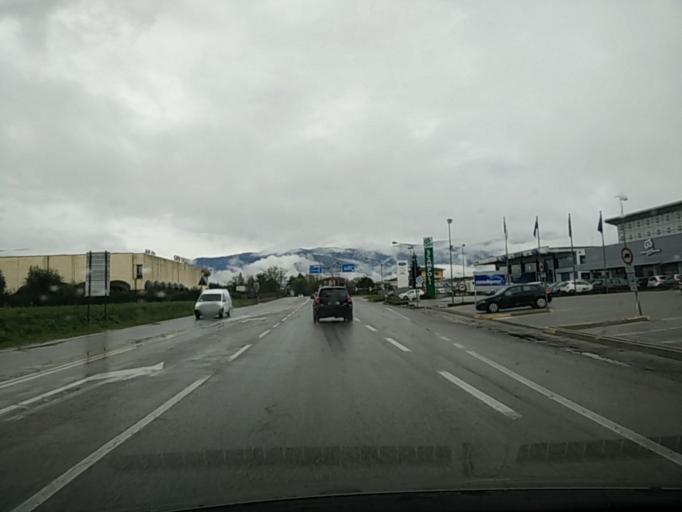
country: IT
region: Veneto
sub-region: Provincia di Vicenza
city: San Zeno-San Giuseppe
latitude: 45.7351
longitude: 11.7600
